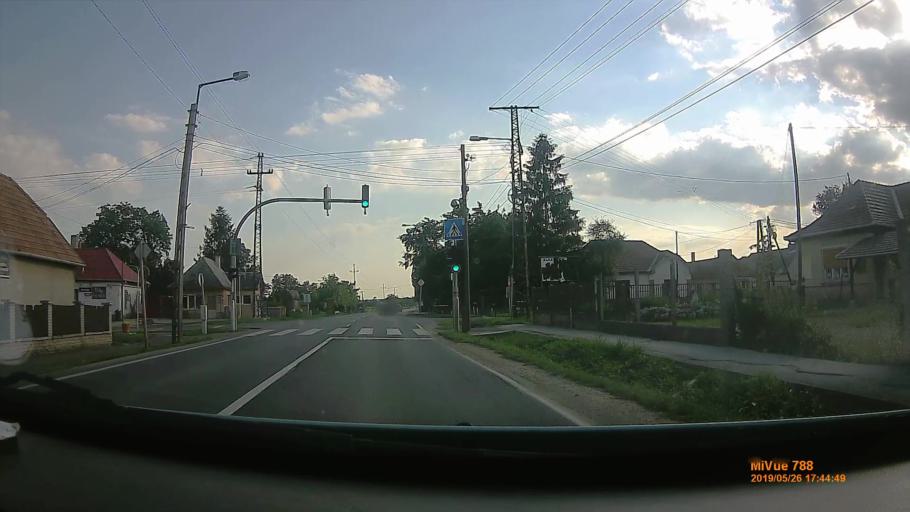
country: HU
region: Borsod-Abauj-Zemplen
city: Aszalo
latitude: 48.2217
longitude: 20.9590
